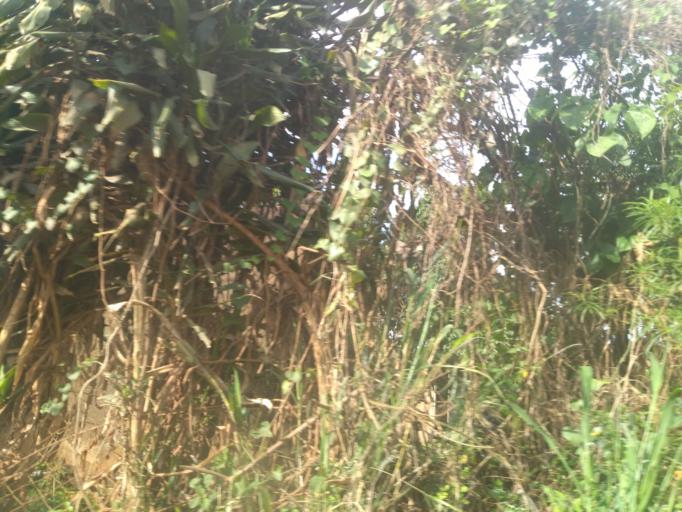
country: UG
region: Central Region
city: Kampala Central Division
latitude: 0.3594
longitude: 32.5777
